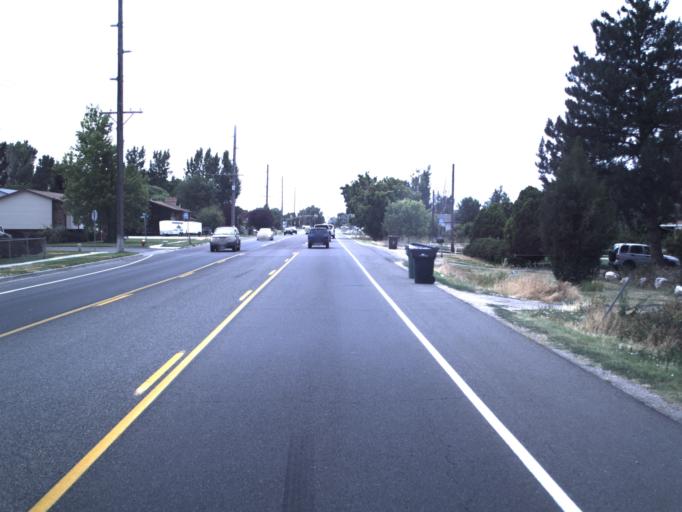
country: US
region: Utah
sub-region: Davis County
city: Clinton
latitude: 41.1658
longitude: -112.0645
